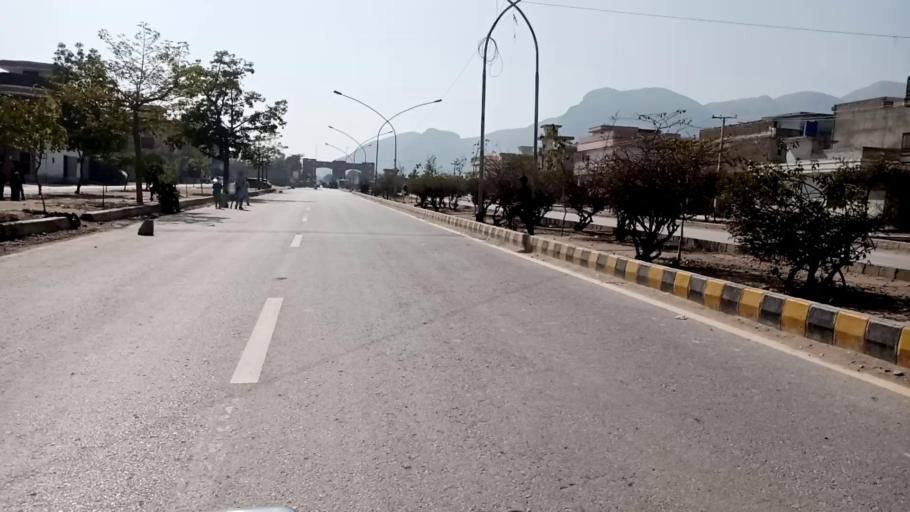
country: PK
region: Khyber Pakhtunkhwa
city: Peshawar
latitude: 33.9504
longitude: 71.4330
